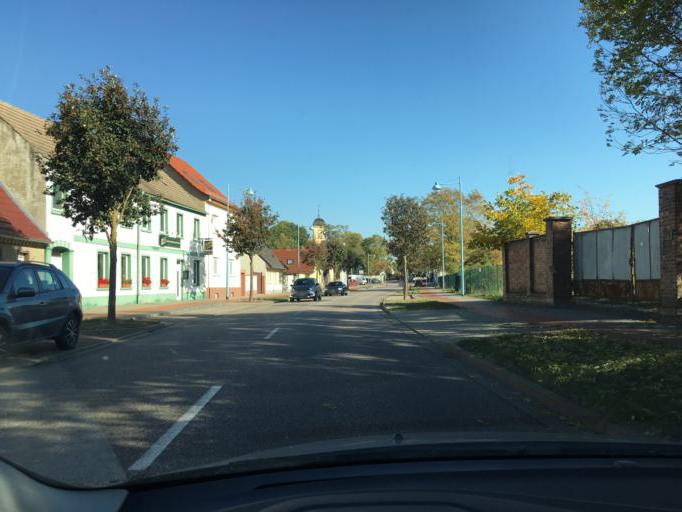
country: DE
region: Saxony-Anhalt
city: Bernburg
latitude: 51.7991
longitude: 11.7708
